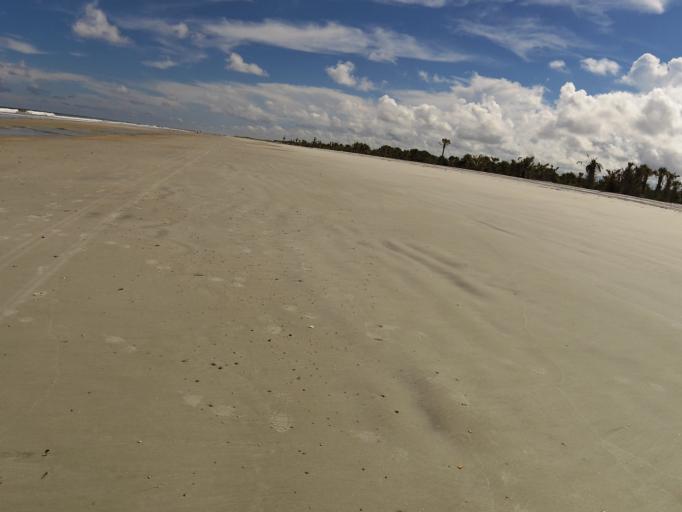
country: US
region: Florida
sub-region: Duval County
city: Atlantic Beach
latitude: 30.4692
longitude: -81.4122
